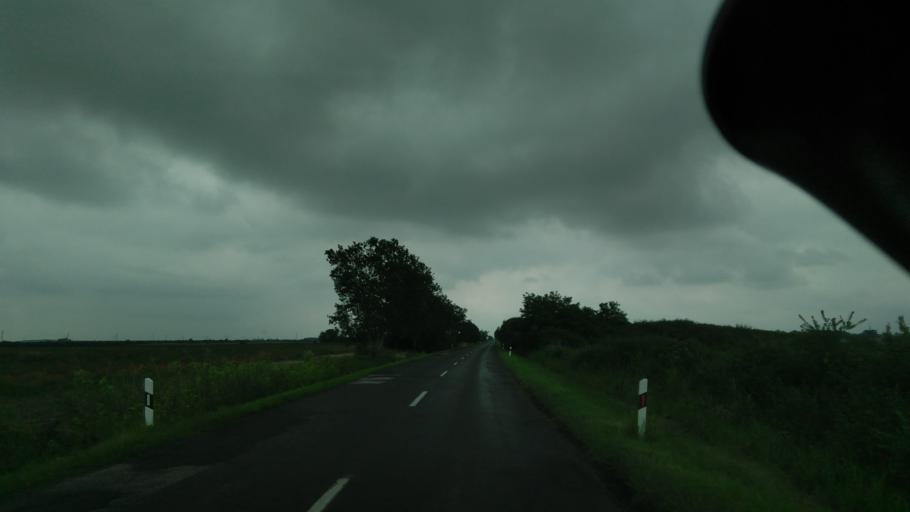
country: HU
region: Bekes
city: Szabadkigyos
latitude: 46.6302
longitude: 21.1036
